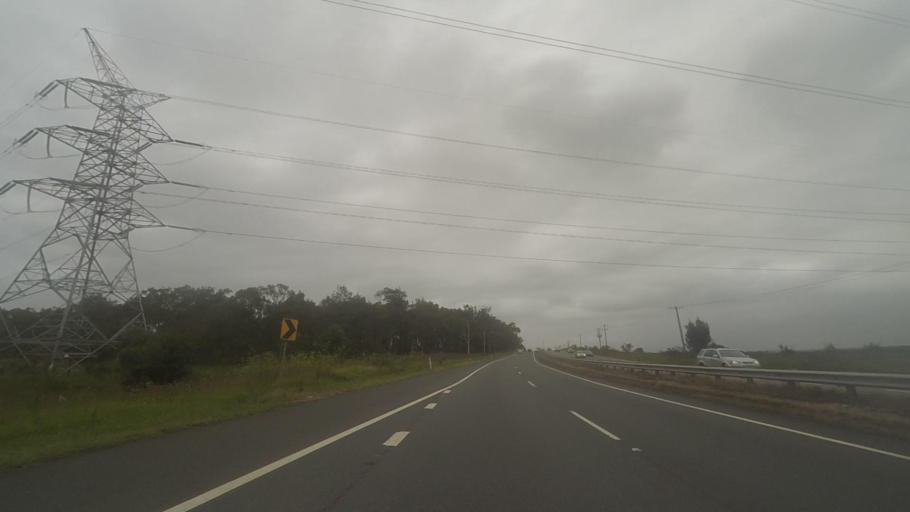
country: AU
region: New South Wales
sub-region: Newcastle
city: Beresfield
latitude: -32.8104
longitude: 151.7092
